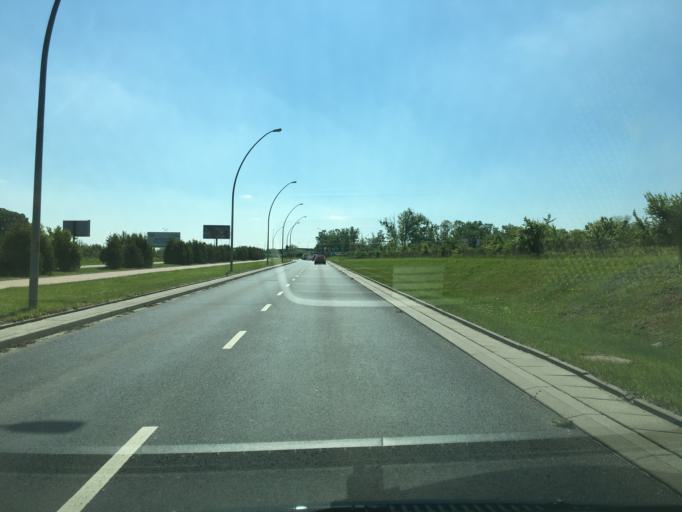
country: PL
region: Lower Silesian Voivodeship
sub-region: Powiat wroclawski
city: Bielany Wroclawskie
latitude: 51.0538
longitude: 16.9621
